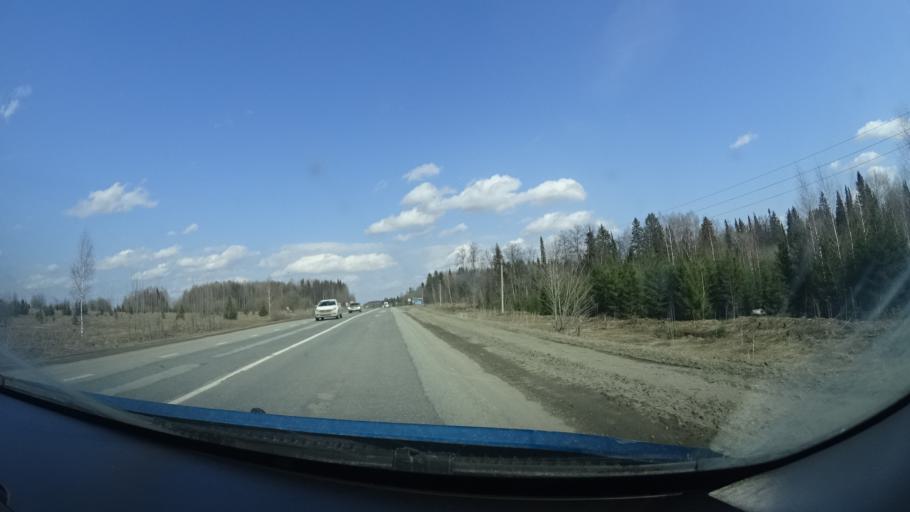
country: RU
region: Perm
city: Kultayevo
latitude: 57.8218
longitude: 55.8040
